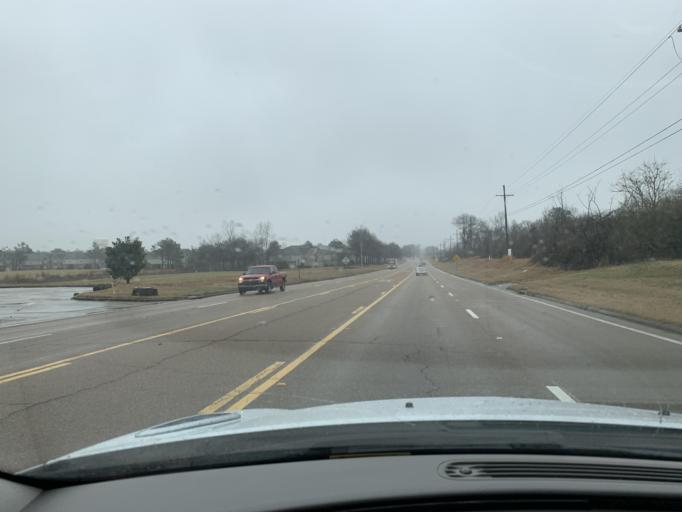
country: US
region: Mississippi
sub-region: De Soto County
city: Horn Lake
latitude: 34.9326
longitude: -90.0130
